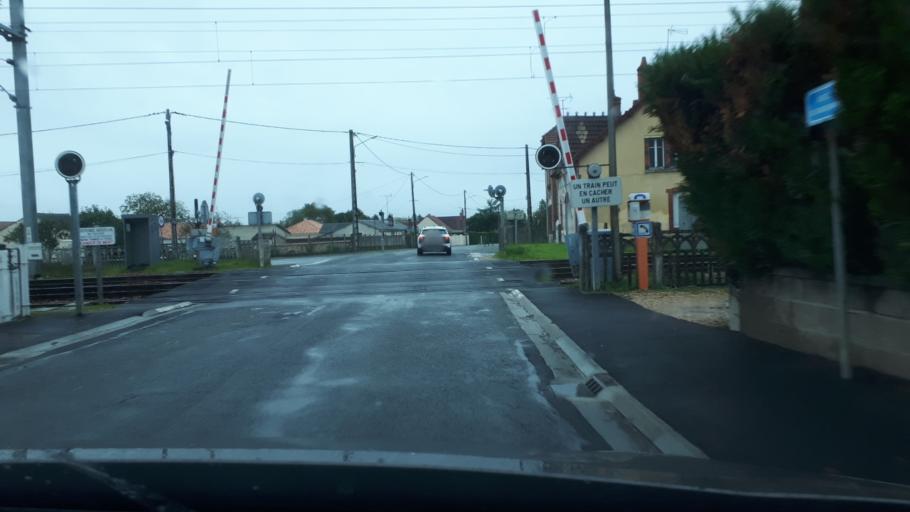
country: FR
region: Centre
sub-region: Departement du Loir-et-Cher
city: Gievres
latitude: 47.2792
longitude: 1.6665
